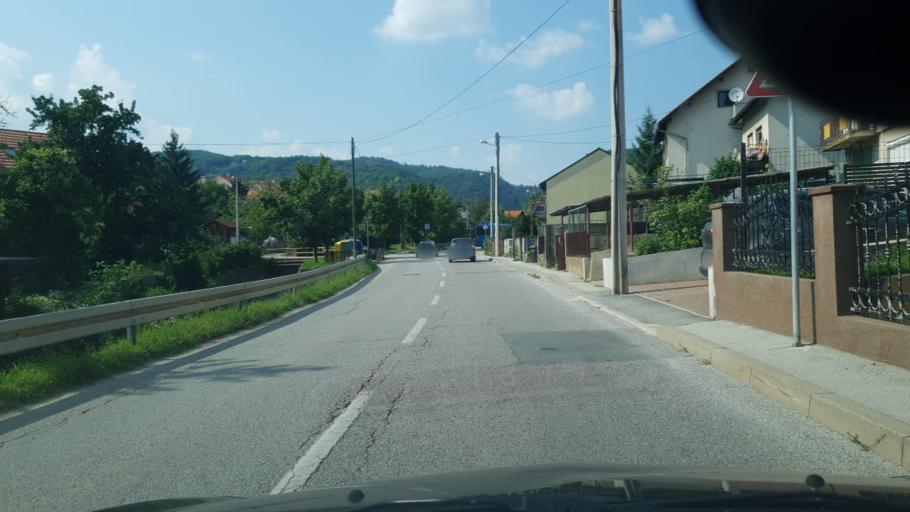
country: HR
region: Grad Zagreb
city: Stenjevec
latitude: 45.8276
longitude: 15.9052
